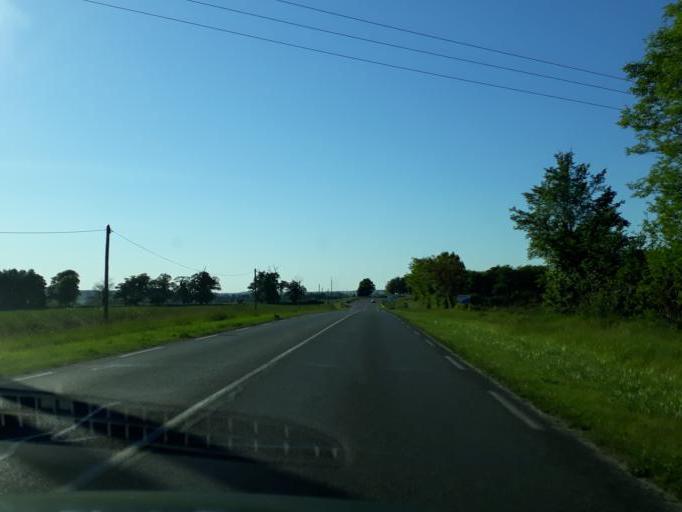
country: FR
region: Centre
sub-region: Departement du Loiret
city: Briare
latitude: 47.6190
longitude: 2.7622
